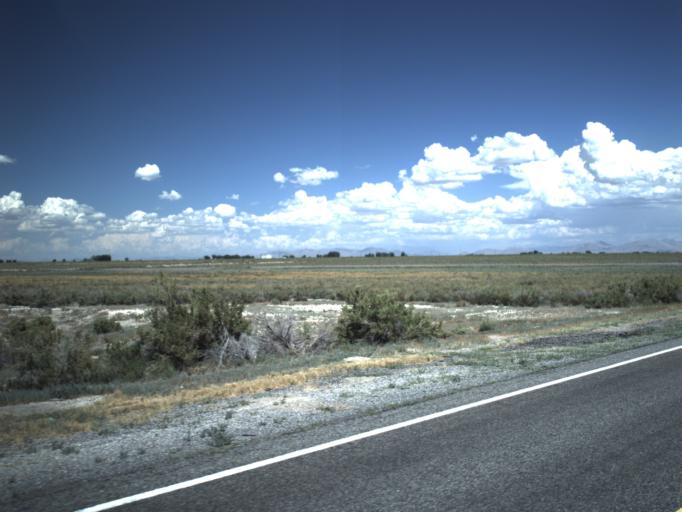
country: US
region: Utah
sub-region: Millard County
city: Delta
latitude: 39.3309
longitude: -112.7119
